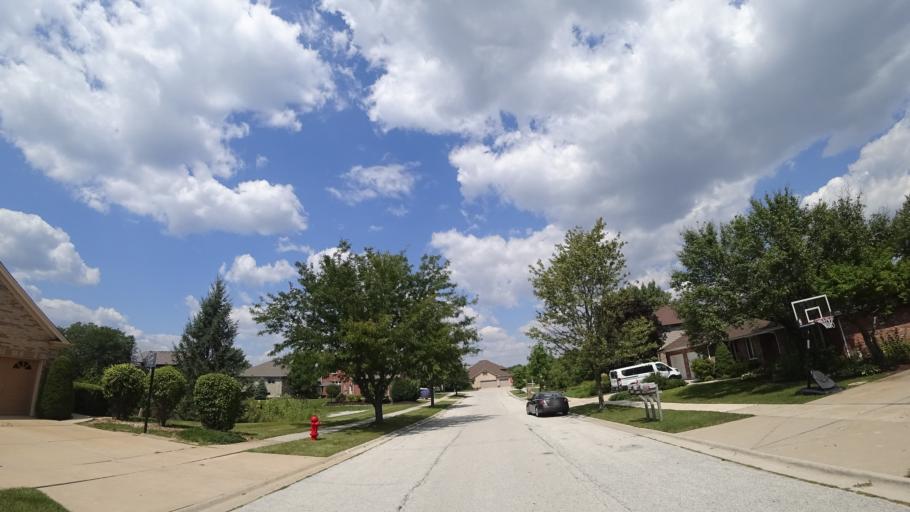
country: US
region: Illinois
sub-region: Cook County
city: Oak Forest
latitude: 41.6195
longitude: -87.7718
